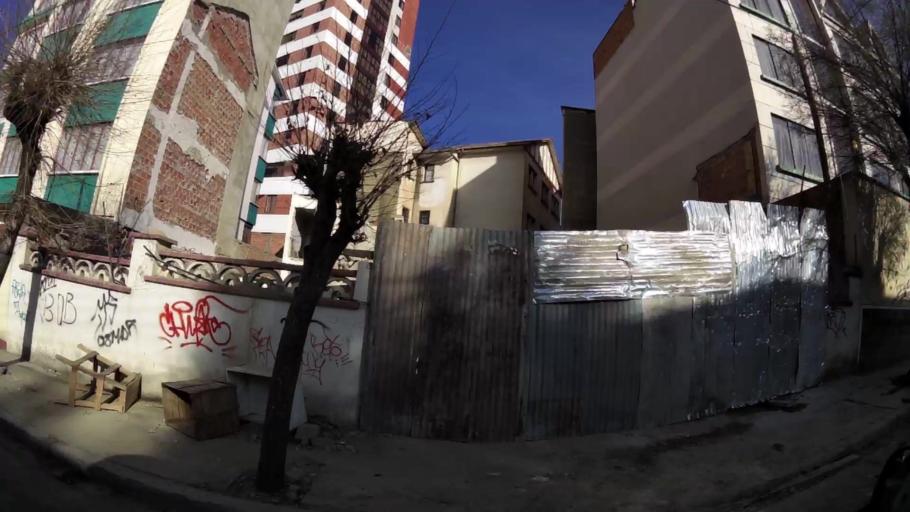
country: BO
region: La Paz
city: La Paz
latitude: -16.5007
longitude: -68.1183
